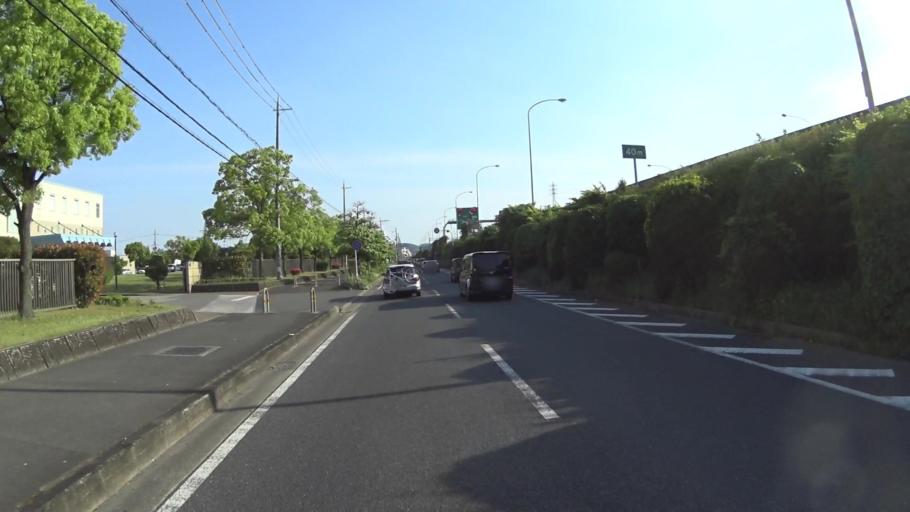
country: JP
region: Kyoto
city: Muko
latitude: 34.9191
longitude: 135.7135
